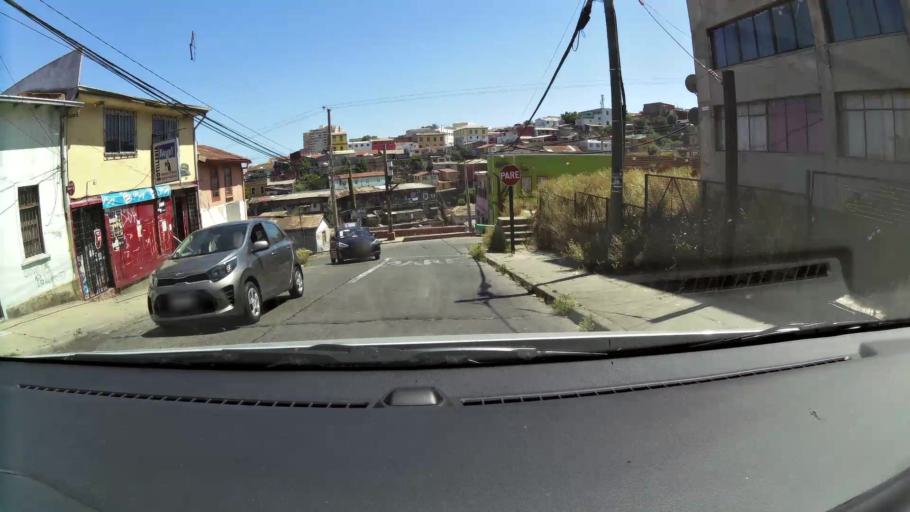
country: CL
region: Valparaiso
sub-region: Provincia de Valparaiso
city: Valparaiso
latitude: -33.0459
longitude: -71.6010
